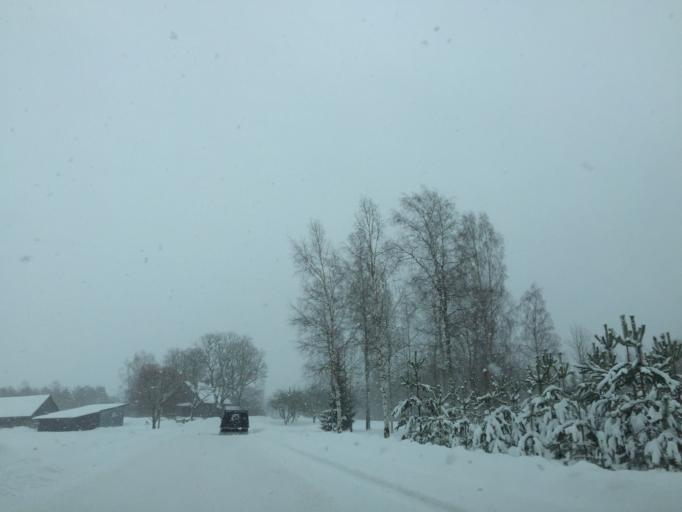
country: LV
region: Amatas Novads
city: Drabesi
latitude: 57.0843
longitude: 25.3789
